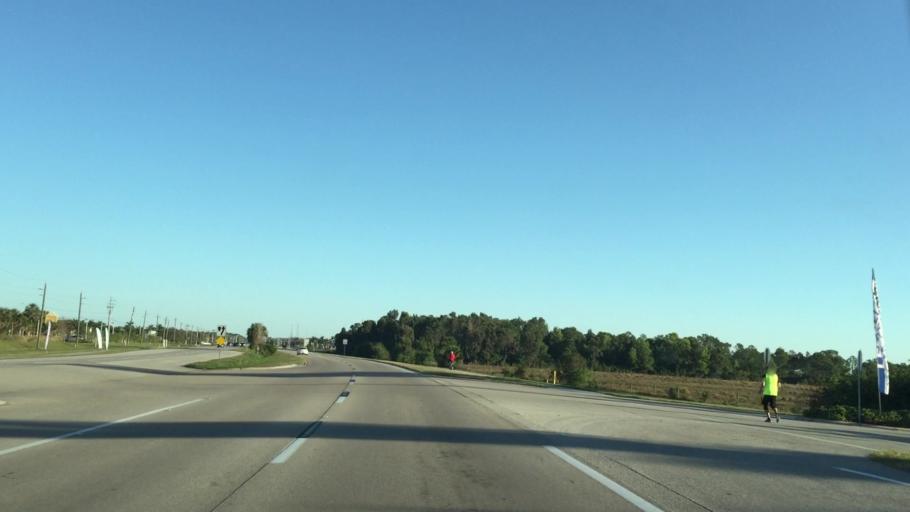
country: US
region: Florida
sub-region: Lee County
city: Fort Myers
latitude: 26.5978
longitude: -81.8111
